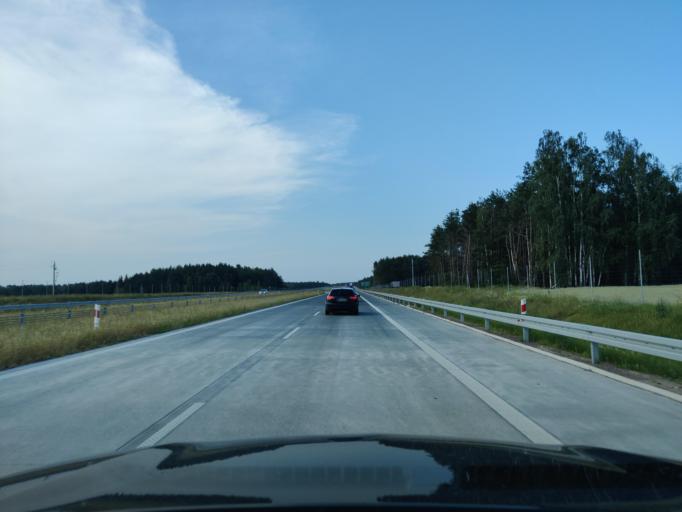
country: PL
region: Masovian Voivodeship
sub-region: Powiat mlawski
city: Strzegowo
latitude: 52.9013
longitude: 20.2697
